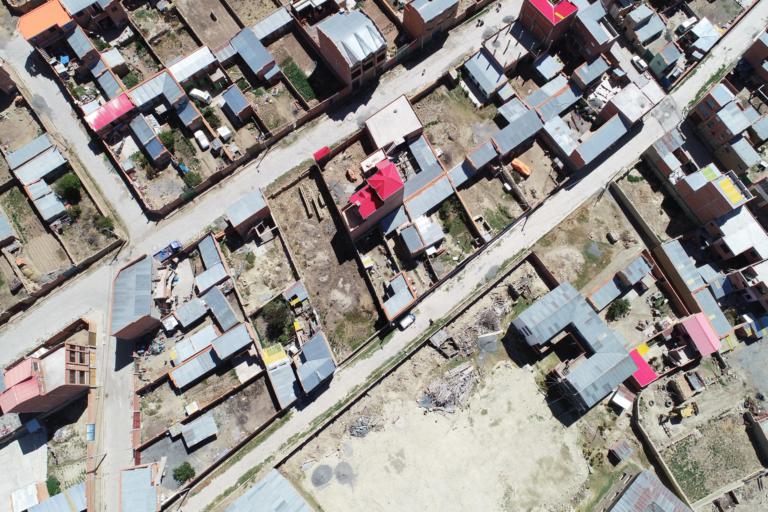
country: BO
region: La Paz
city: Achacachi
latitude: -16.0460
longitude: -68.6811
